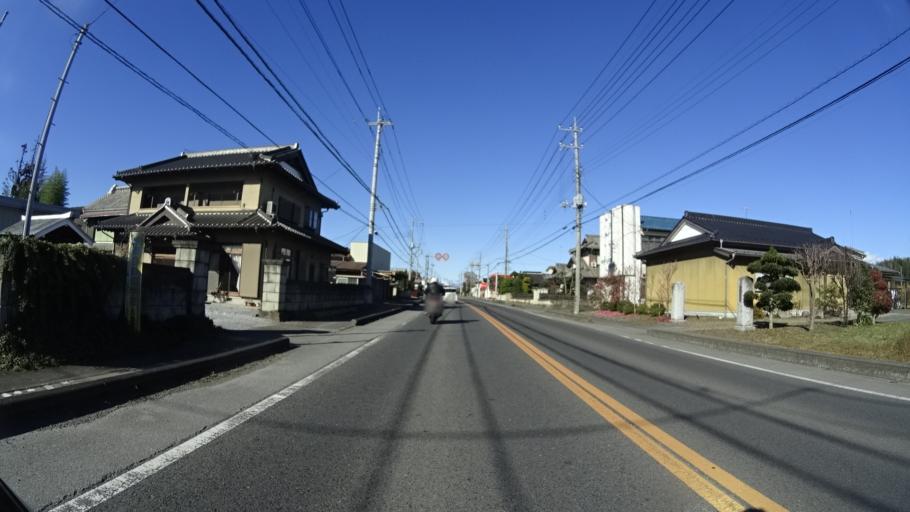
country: JP
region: Tochigi
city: Kanuma
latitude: 36.5195
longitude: 139.7512
